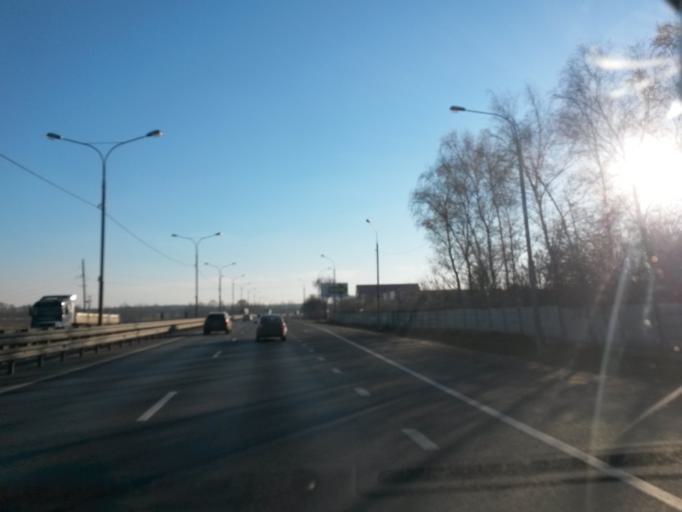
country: RU
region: Moskovskaya
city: Pushkino
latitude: 56.0063
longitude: 37.8778
